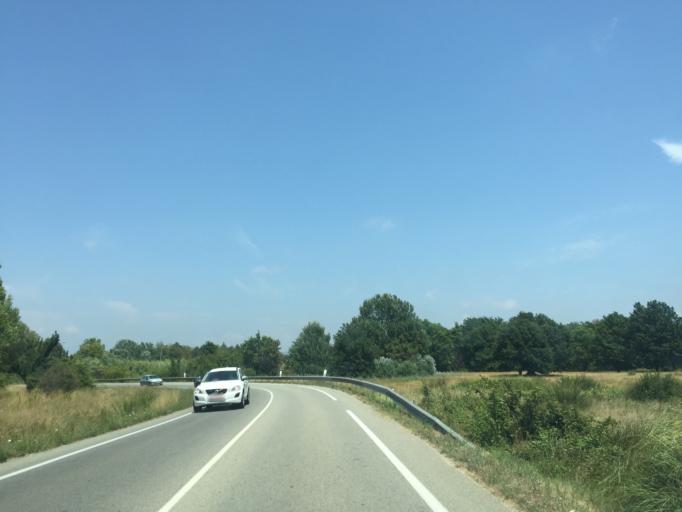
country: FR
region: Provence-Alpes-Cote d'Azur
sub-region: Departement du Var
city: Puget-sur-Argens
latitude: 43.4113
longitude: 6.6869
